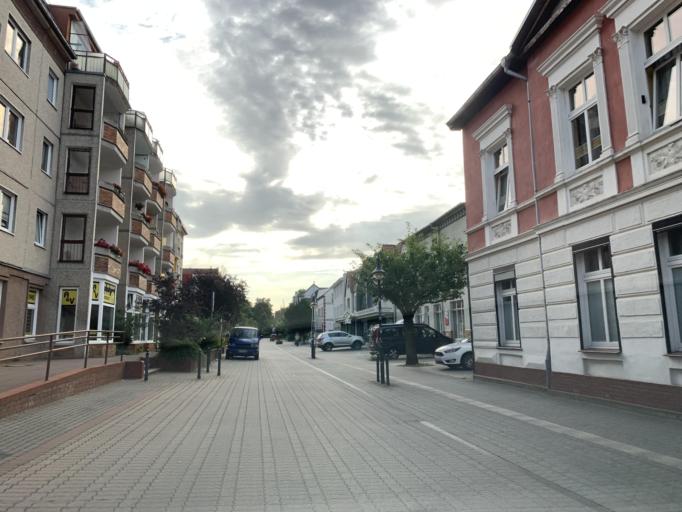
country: DE
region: Mecklenburg-Vorpommern
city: Neubrandenburg
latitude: 53.5564
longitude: 13.2699
